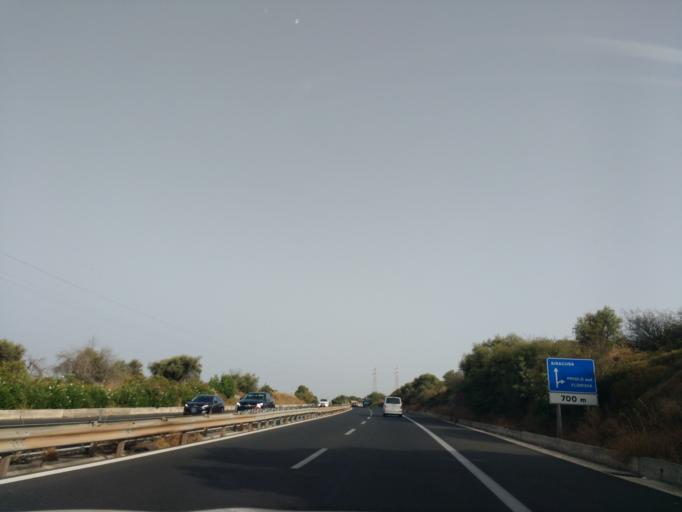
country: IT
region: Sicily
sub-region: Provincia di Siracusa
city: Priolo Gargallo
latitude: 37.1380
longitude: 15.1693
